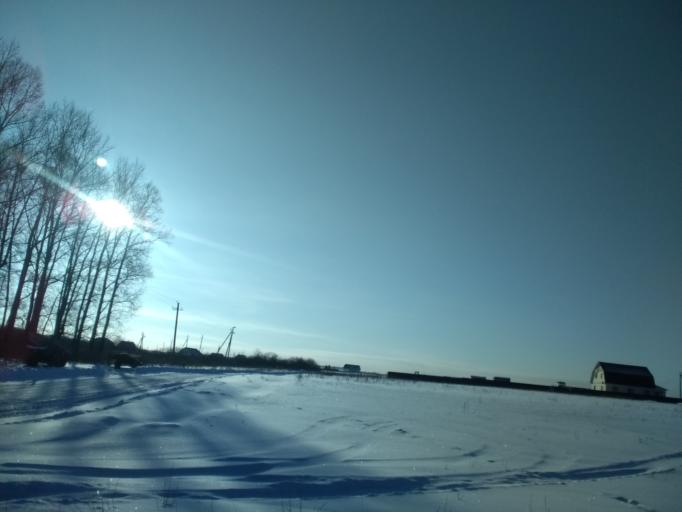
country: RU
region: Bashkortostan
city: Kudeyevskiy
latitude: 54.6832
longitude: 56.6078
